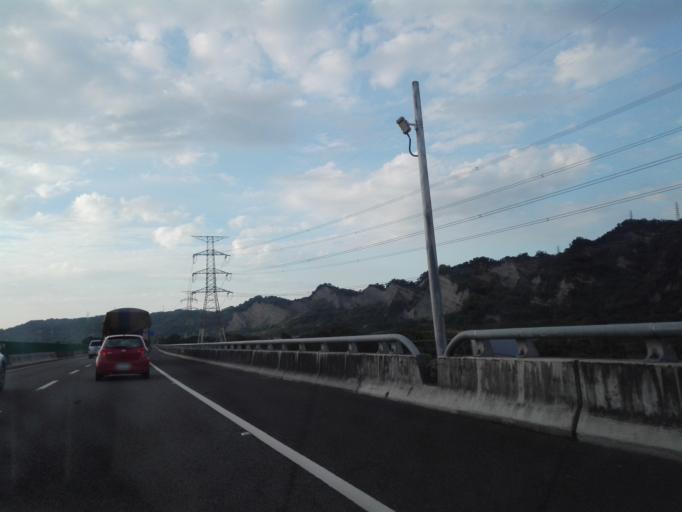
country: TW
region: Taiwan
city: Zhongxing New Village
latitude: 23.9985
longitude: 120.7415
